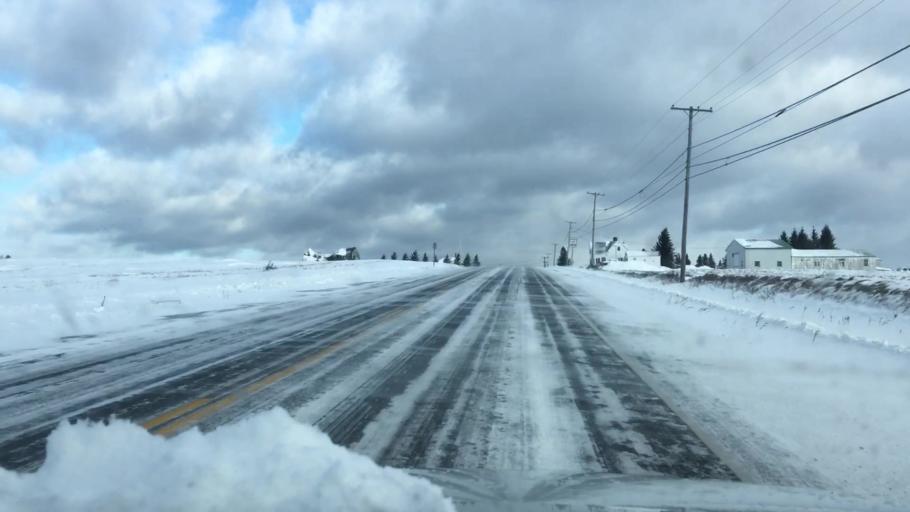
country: US
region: Maine
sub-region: Aroostook County
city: Caribou
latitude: 46.9356
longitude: -68.0233
